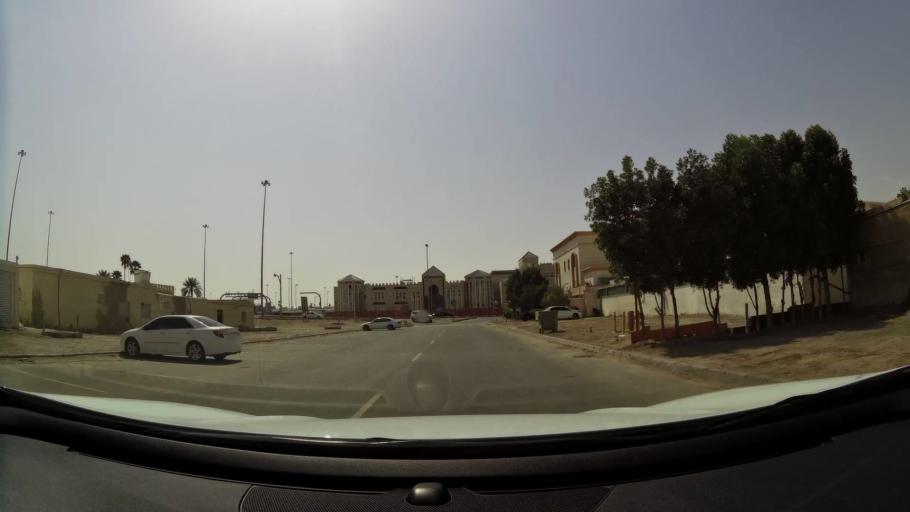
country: AE
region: Abu Dhabi
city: Abu Dhabi
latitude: 24.2847
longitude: 54.6501
